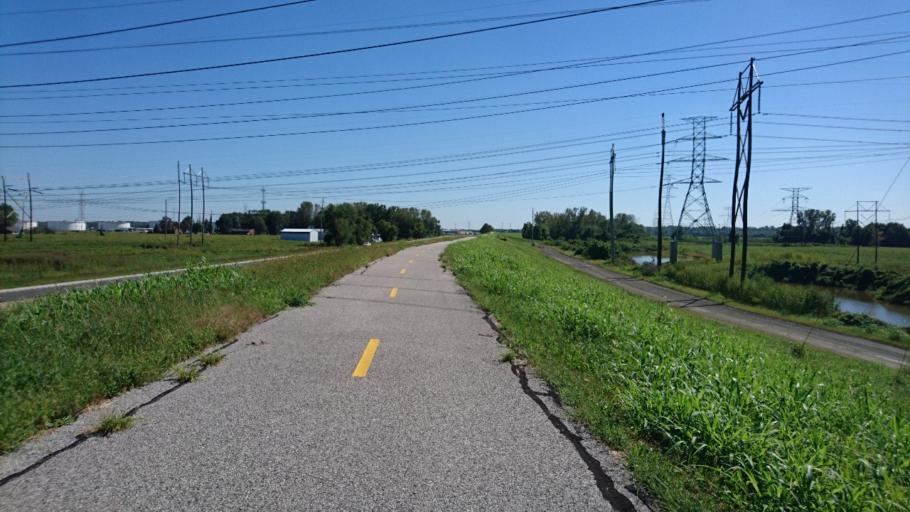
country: US
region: Illinois
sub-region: Madison County
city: Hartford
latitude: 38.8261
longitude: -90.1006
